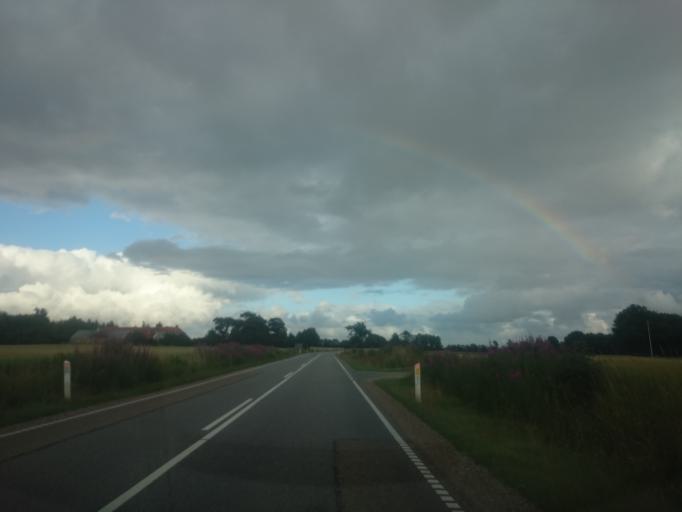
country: DK
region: South Denmark
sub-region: Billund Kommune
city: Grindsted
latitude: 55.6620
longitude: 8.7716
